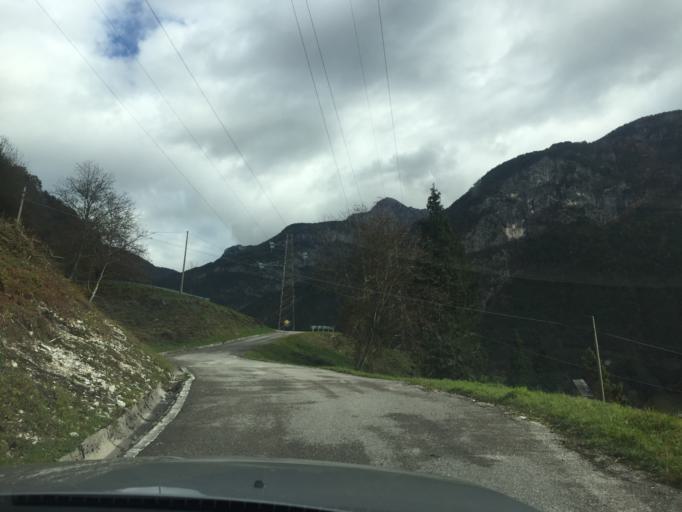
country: IT
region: Friuli Venezia Giulia
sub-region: Provincia di Udine
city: Chiusaforte
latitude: 46.4087
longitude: 13.3077
